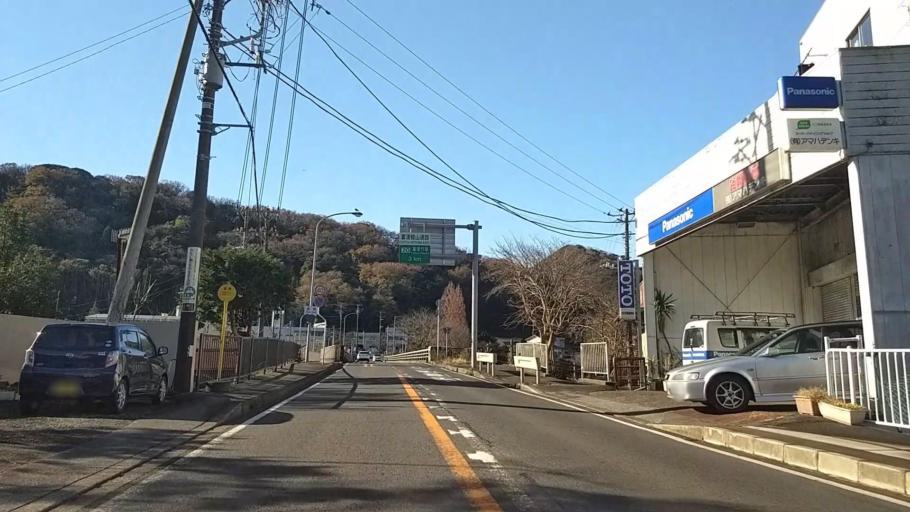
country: JP
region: Chiba
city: Futtsu
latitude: 35.2157
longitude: 139.8701
